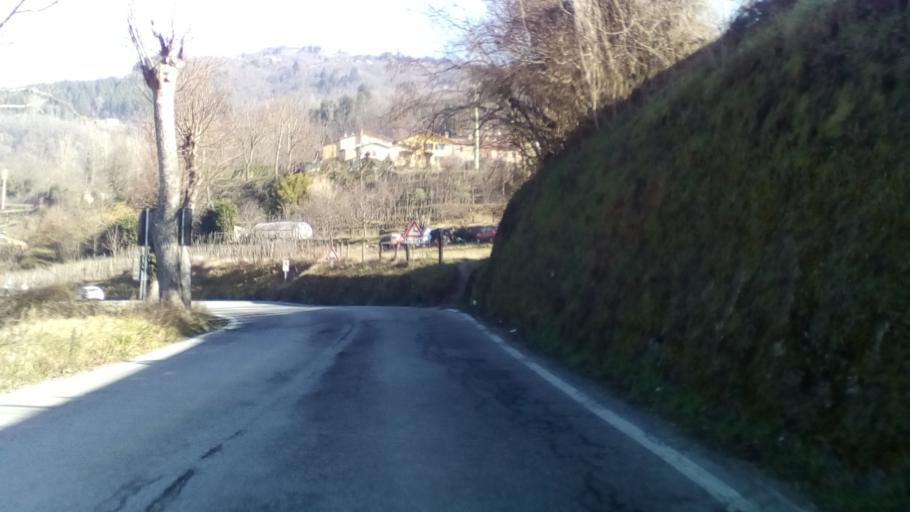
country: IT
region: Tuscany
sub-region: Provincia di Lucca
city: Pieve Fosciana
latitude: 44.1379
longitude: 10.4177
